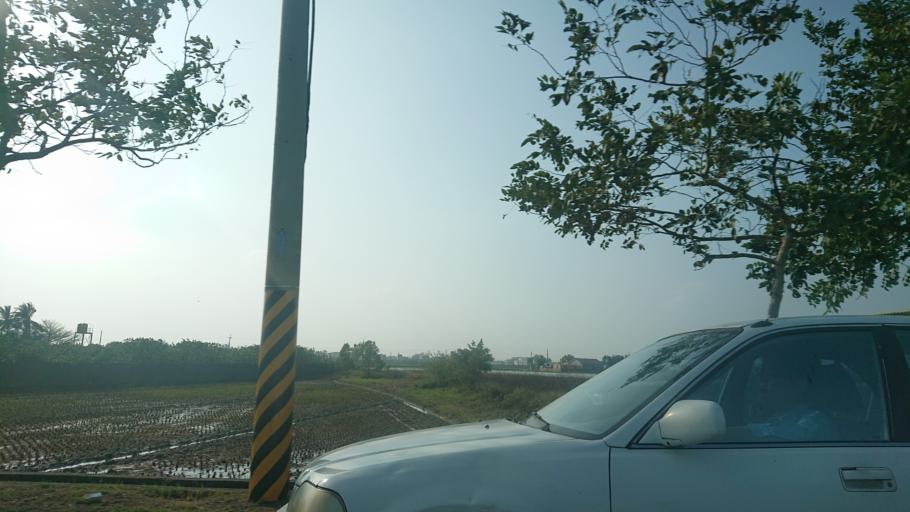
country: TW
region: Taiwan
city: Xinying
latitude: 23.2061
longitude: 120.2719
